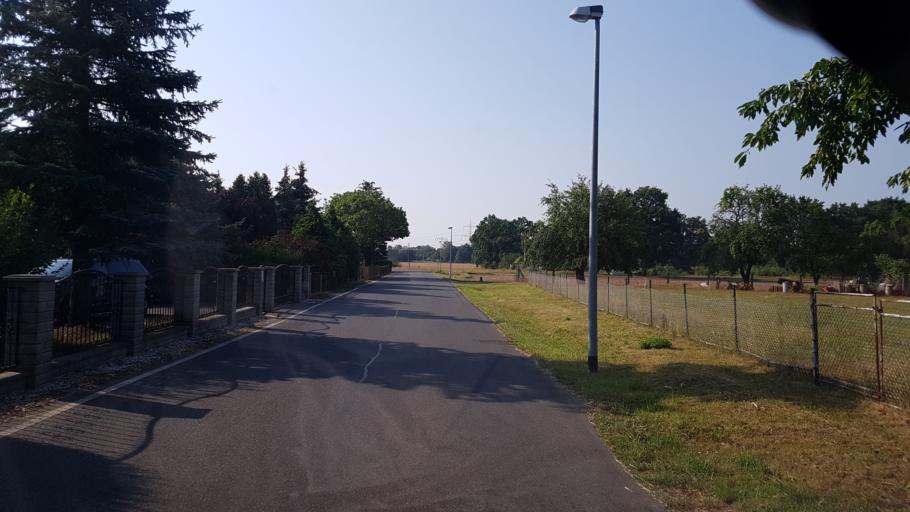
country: DE
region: Brandenburg
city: Drebkau
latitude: 51.6698
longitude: 14.2331
